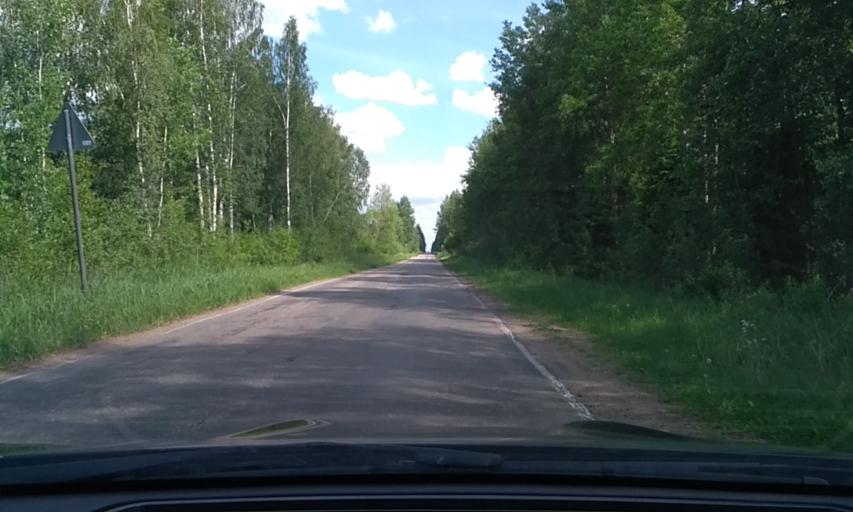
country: RU
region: Leningrad
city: Imeni Sverdlova
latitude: 59.8229
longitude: 30.7447
